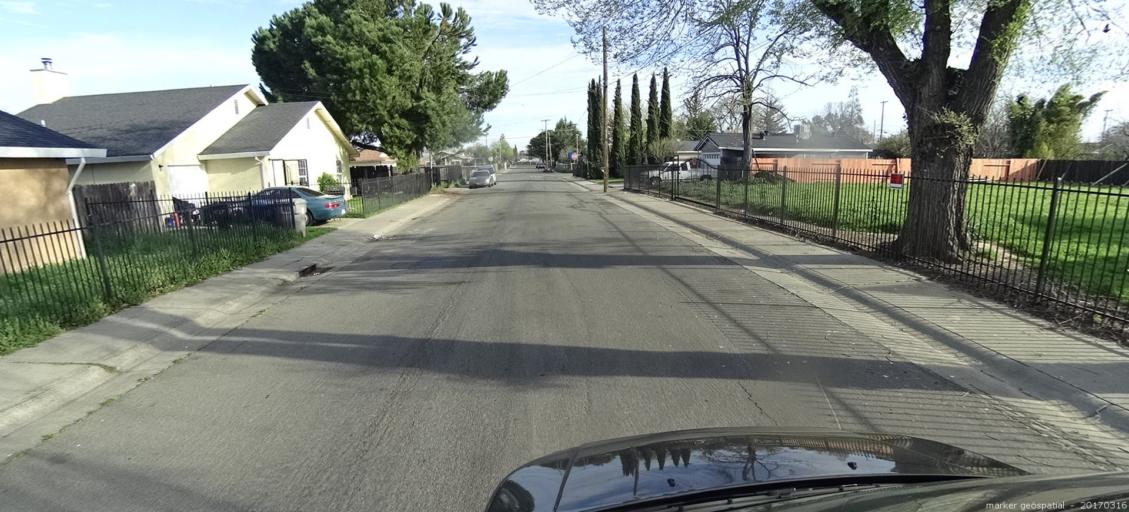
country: US
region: California
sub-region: Sacramento County
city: Parkway
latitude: 38.5004
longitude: -121.4774
